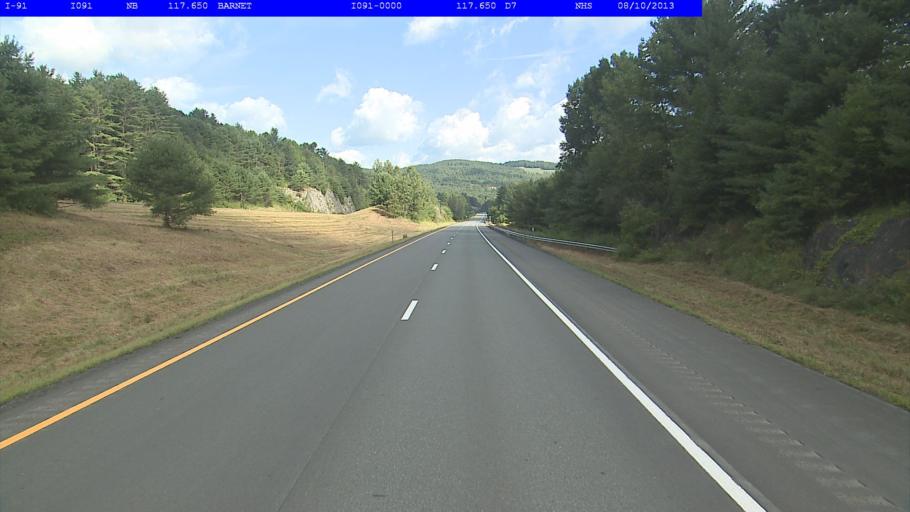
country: US
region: New Hampshire
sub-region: Grafton County
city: Woodsville
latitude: 44.2611
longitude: -72.0666
